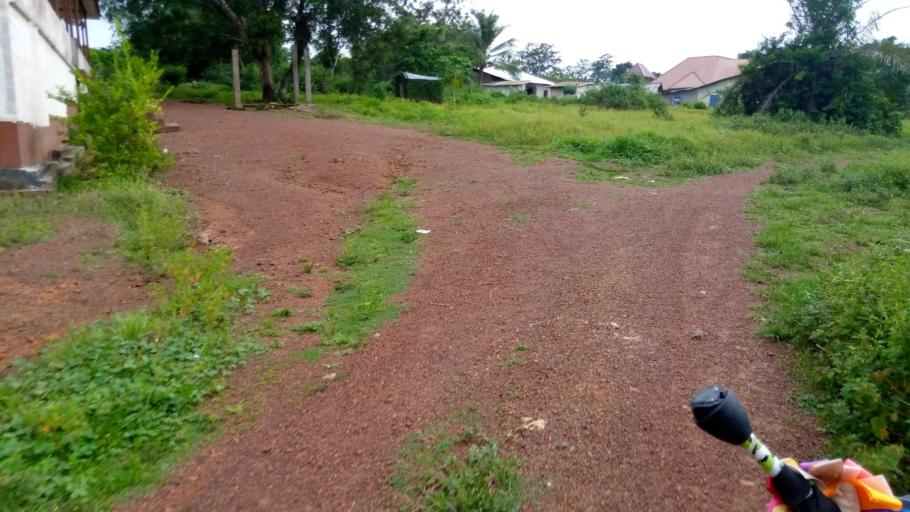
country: SL
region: Southern Province
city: Moyamba
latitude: 8.1622
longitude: -12.4404
